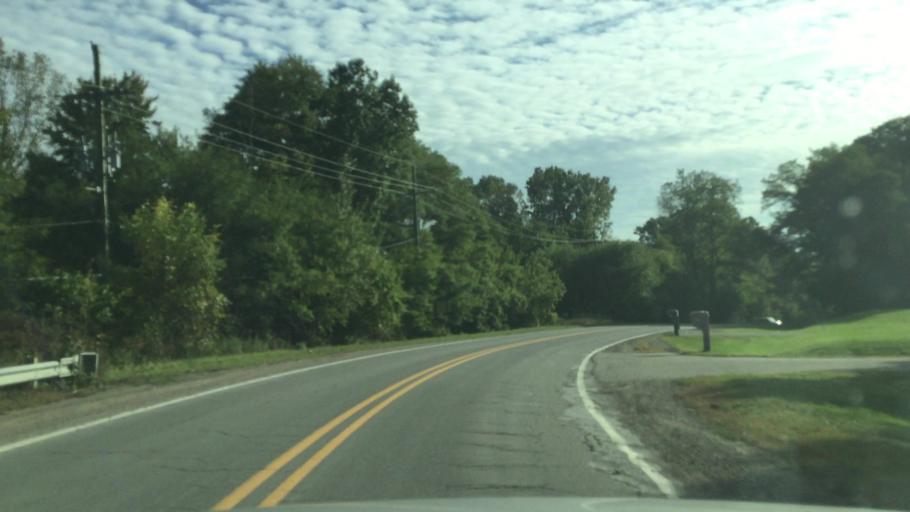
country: US
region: Michigan
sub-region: Livingston County
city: Howell
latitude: 42.6007
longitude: -83.8670
